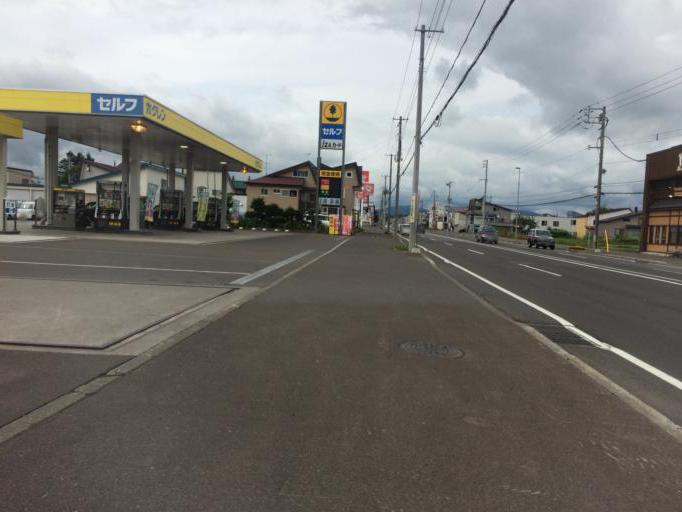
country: JP
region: Hokkaido
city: Niseko Town
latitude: 42.8931
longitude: 140.7517
